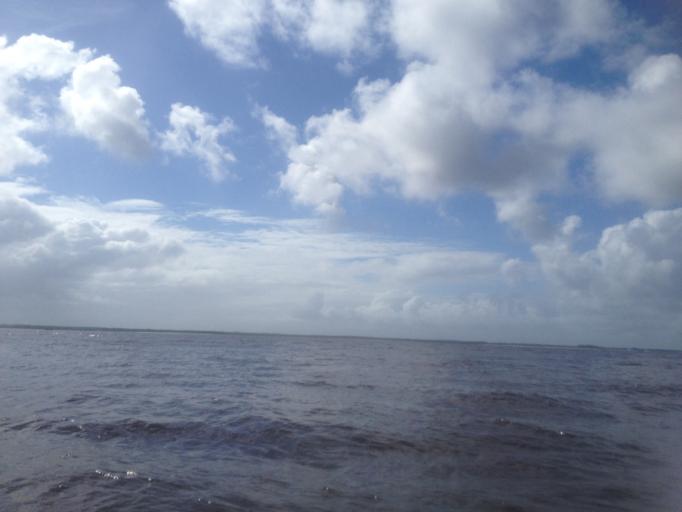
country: BR
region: Sergipe
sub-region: Indiaroba
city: Indiaroba
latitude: -11.4656
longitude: -37.3710
